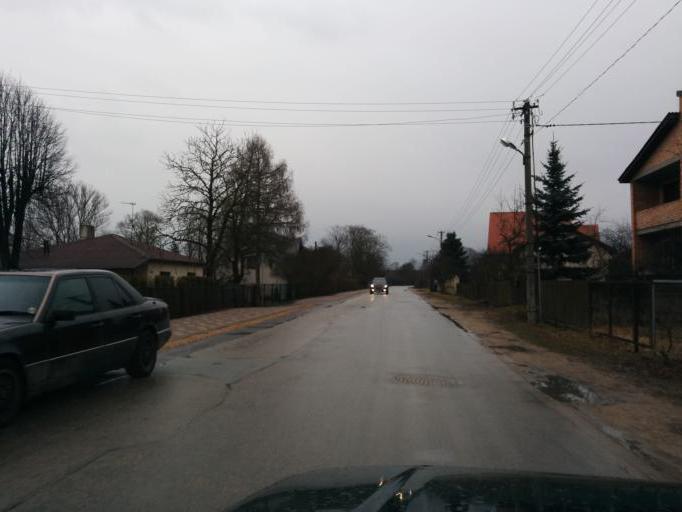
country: LV
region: Kekava
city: Balozi
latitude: 56.8744
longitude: 24.1816
